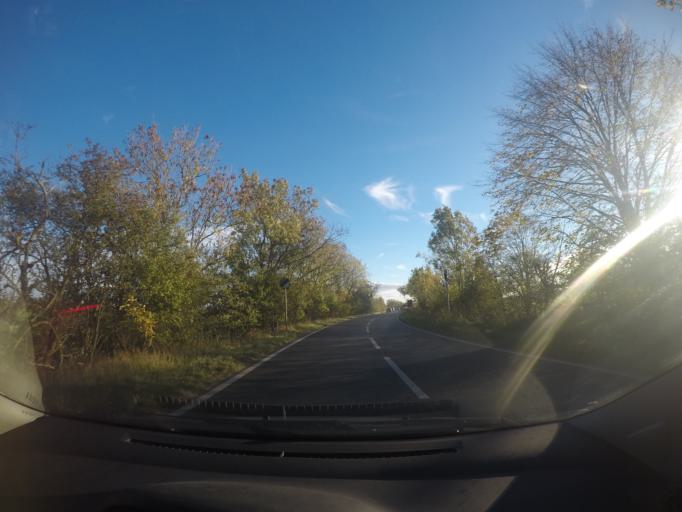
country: GB
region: England
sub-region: City of York
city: Wigginton
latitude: 53.9883
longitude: -1.0855
